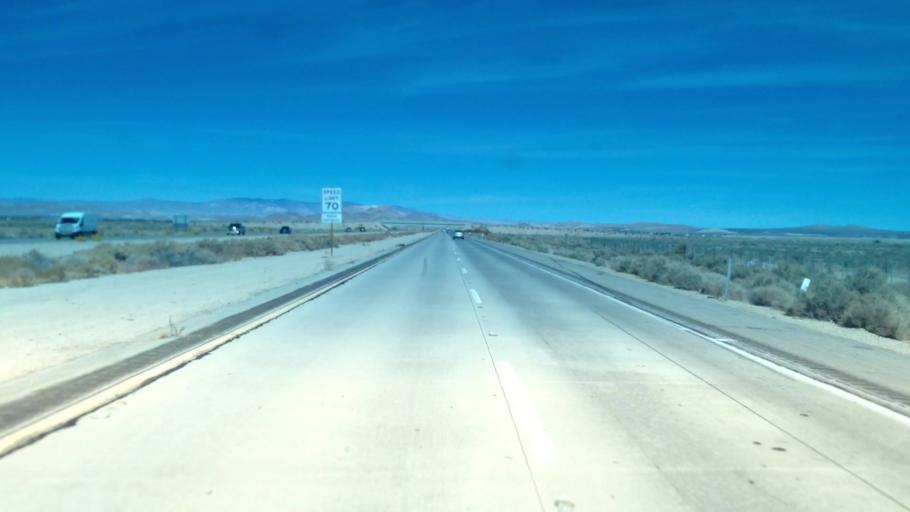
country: US
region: California
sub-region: Kern County
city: Rosamond
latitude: 34.7844
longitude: -118.1705
